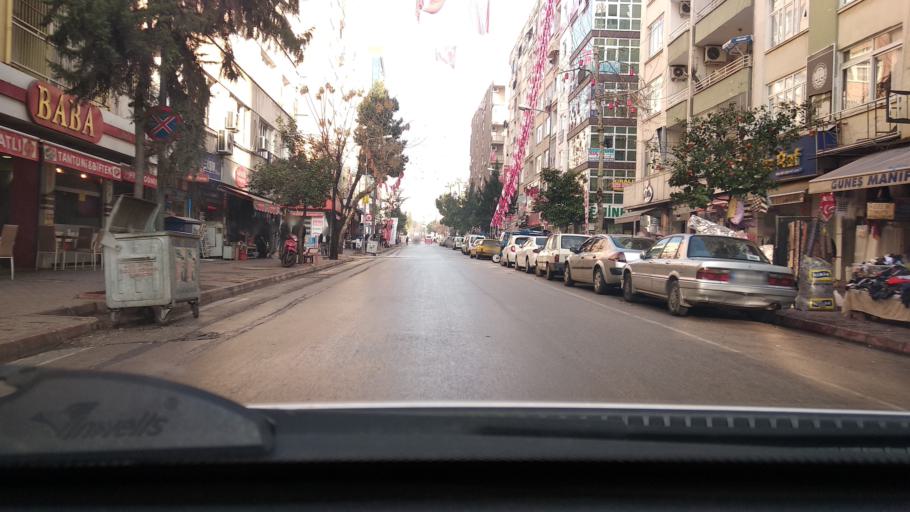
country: TR
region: Mersin
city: Mercin
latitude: 36.8065
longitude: 34.6226
